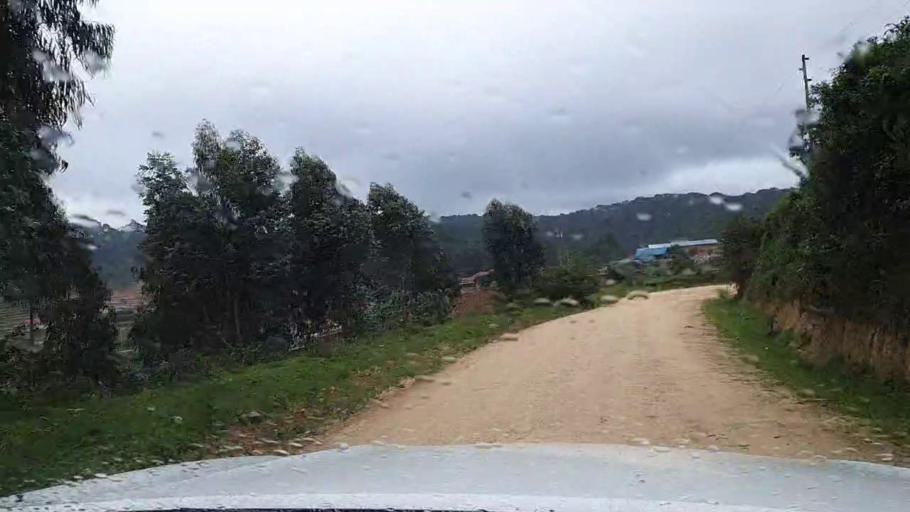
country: RW
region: Southern Province
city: Nzega
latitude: -2.3703
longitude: 29.3829
